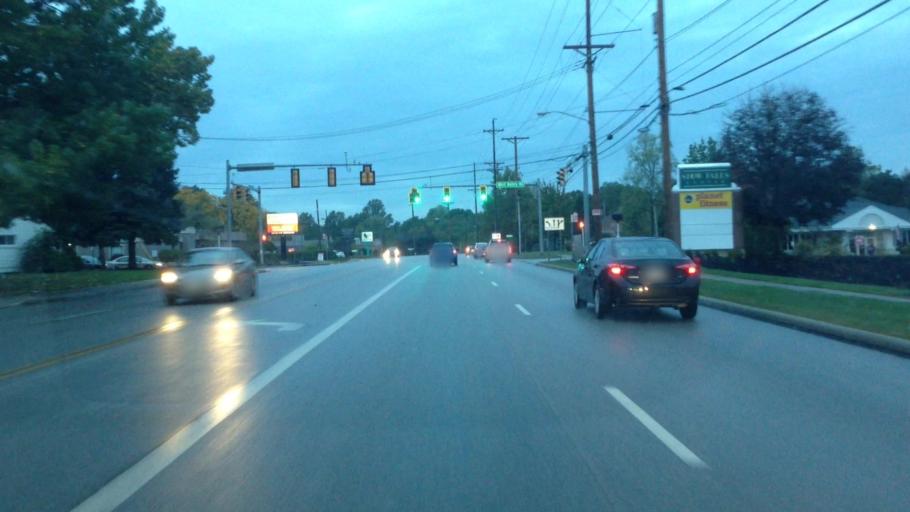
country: US
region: Ohio
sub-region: Summit County
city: Silver Lake
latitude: 41.1633
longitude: -81.4826
